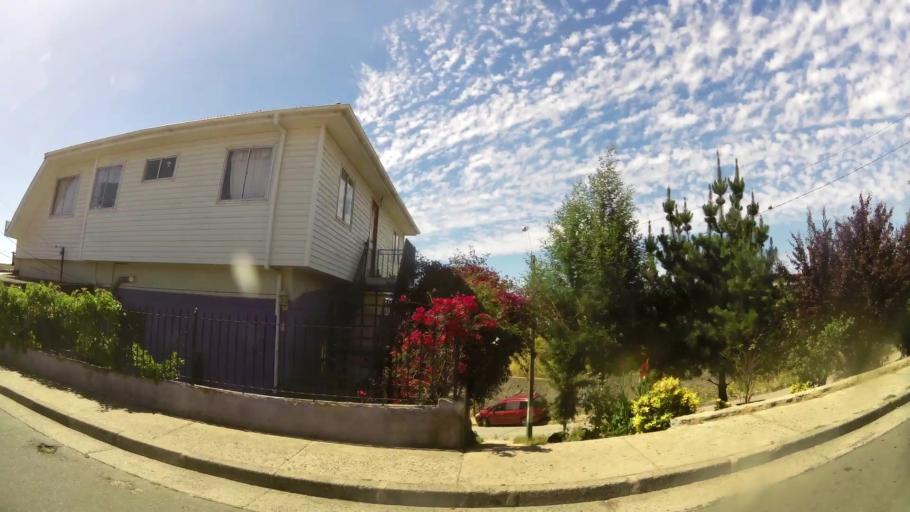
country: CL
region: Valparaiso
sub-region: Provincia de Valparaiso
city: Vina del Mar
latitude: -33.0417
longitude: -71.5791
